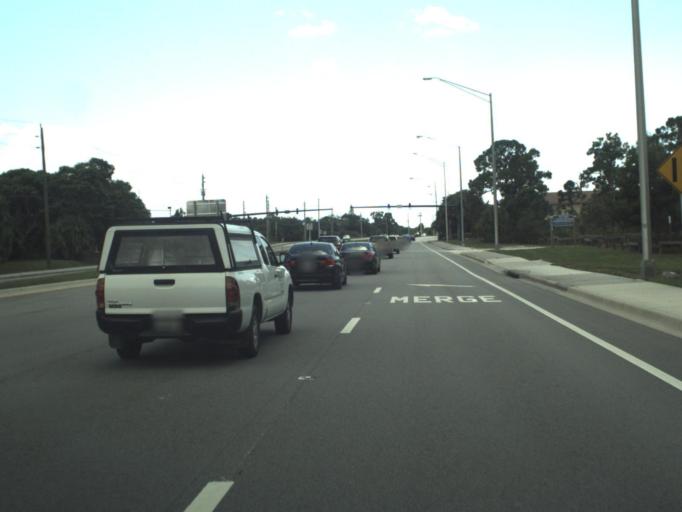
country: US
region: Florida
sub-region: Martin County
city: Palm City
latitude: 27.1570
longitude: -80.2465
